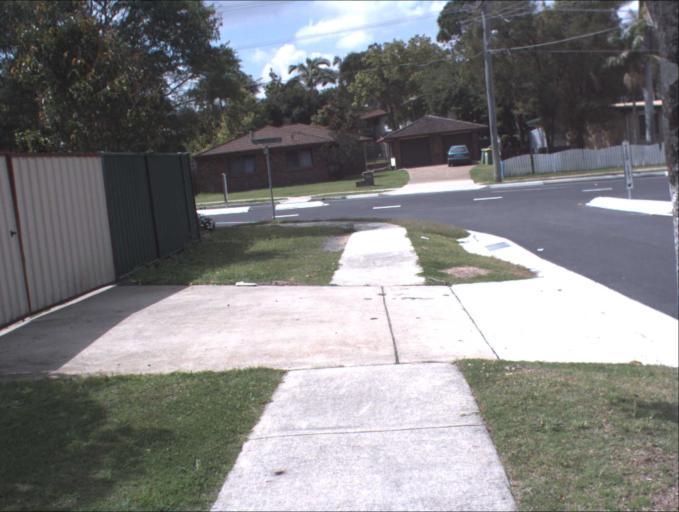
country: AU
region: Queensland
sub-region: Brisbane
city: Sunnybank Hills
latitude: -27.6590
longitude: 153.0524
